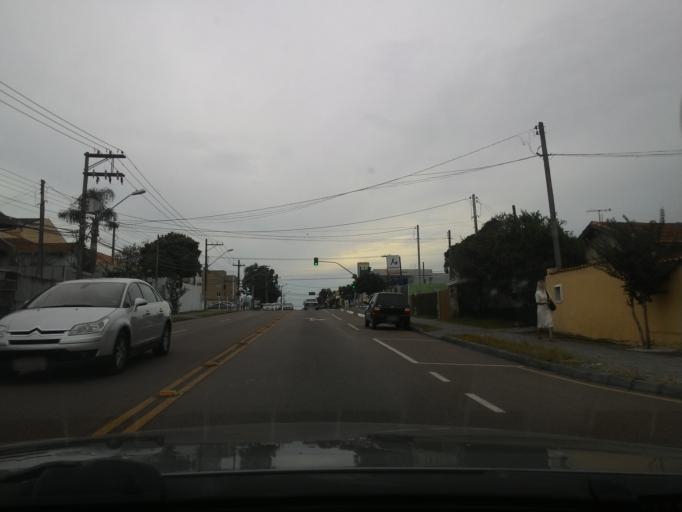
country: BR
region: Parana
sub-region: Pinhais
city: Pinhais
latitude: -25.4436
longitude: -49.2226
